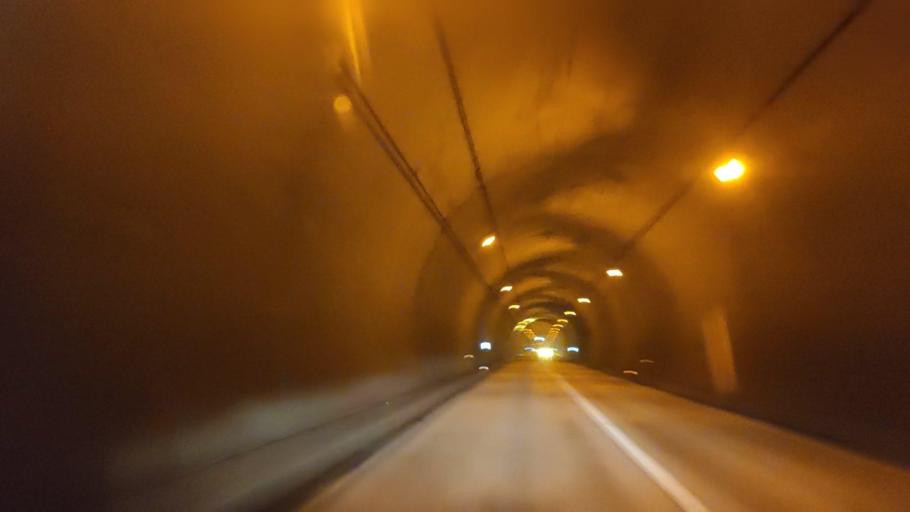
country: JP
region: Tottori
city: Kurayoshi
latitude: 35.3106
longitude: 133.7500
